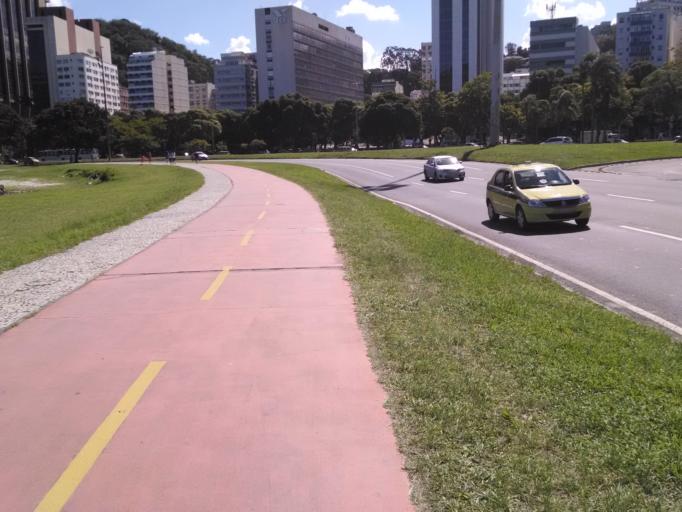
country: BR
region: Rio de Janeiro
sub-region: Rio De Janeiro
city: Rio de Janeiro
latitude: -22.9430
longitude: -43.1776
